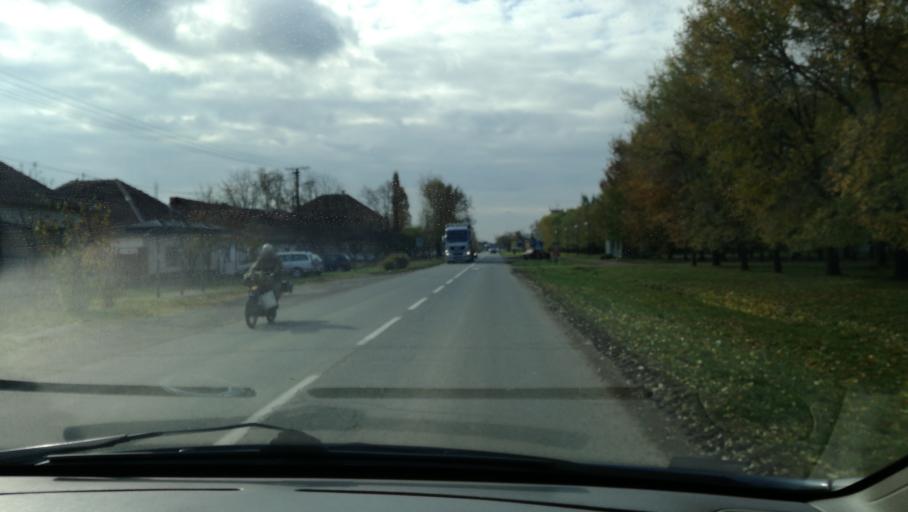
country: RS
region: Autonomna Pokrajina Vojvodina
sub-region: Severnobanatski Okrug
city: Kikinda
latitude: 45.8377
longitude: 20.4527
